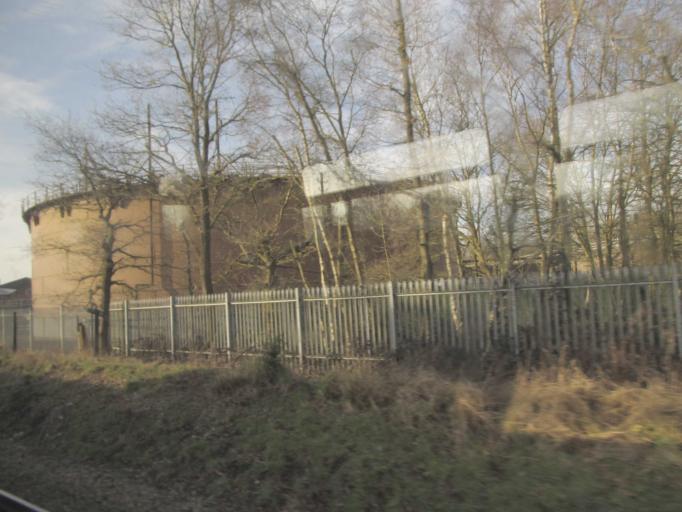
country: GB
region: England
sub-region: Hampshire
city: Farnborough
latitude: 51.2803
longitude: -0.7333
